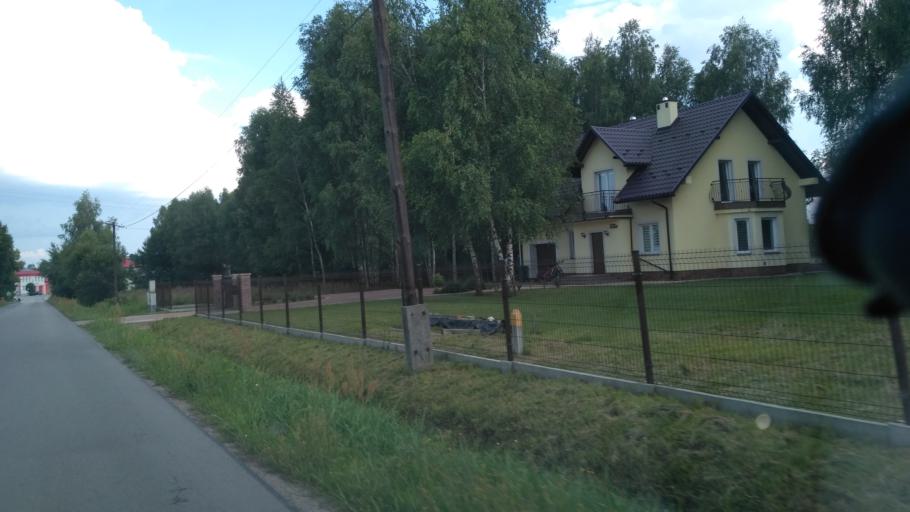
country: PL
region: Subcarpathian Voivodeship
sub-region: Powiat rzeszowski
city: Wysoka Glogowska
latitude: 50.1599
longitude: 22.0170
